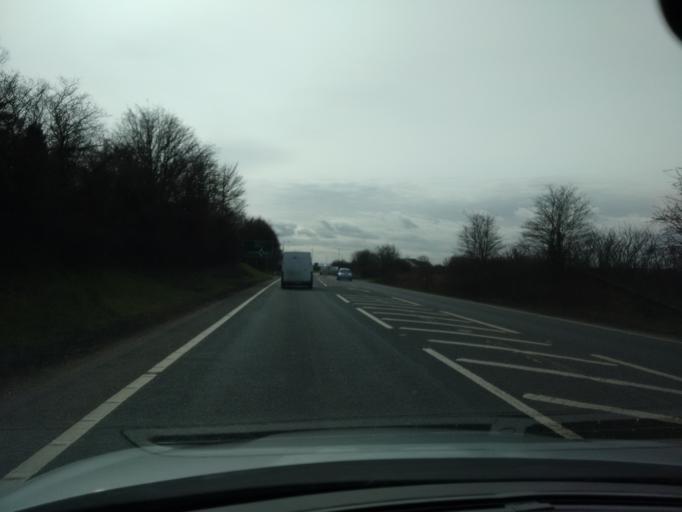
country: GB
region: England
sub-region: Worcestershire
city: Badsey
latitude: 52.0946
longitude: -1.9218
